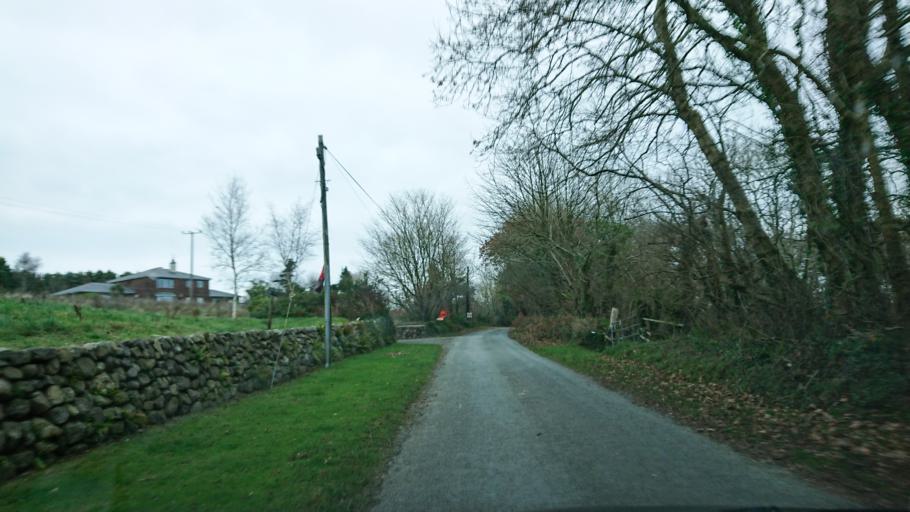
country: IE
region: Munster
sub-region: Waterford
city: Dunmore East
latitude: 52.1981
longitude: -7.0298
